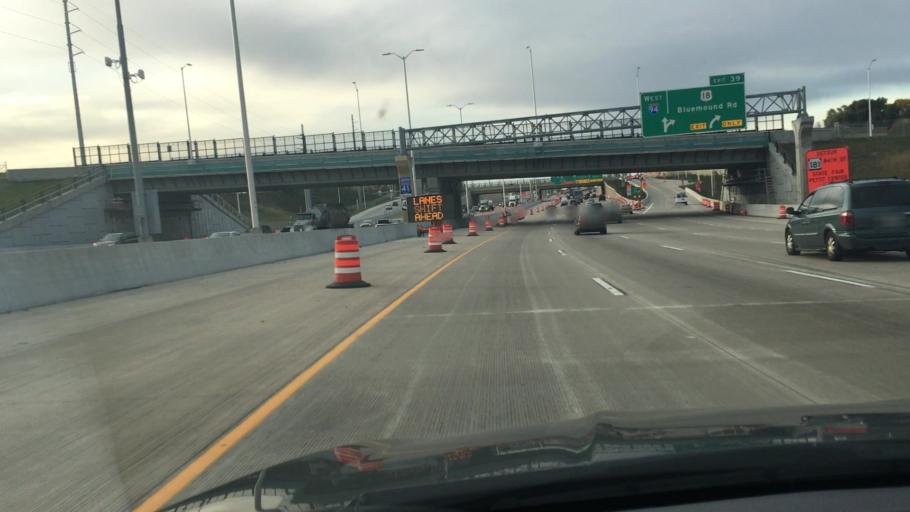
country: US
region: Wisconsin
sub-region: Milwaukee County
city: Wauwatosa
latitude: 43.0393
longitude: -88.0331
